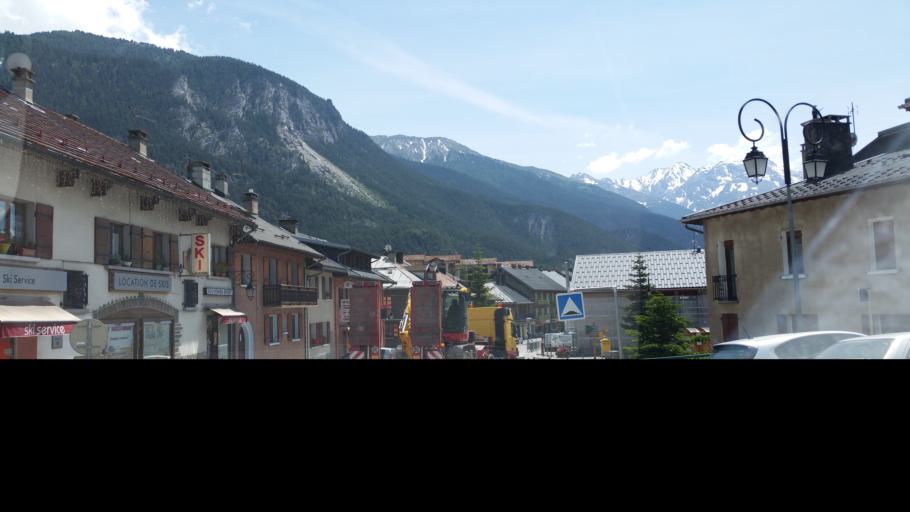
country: FR
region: Rhone-Alpes
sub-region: Departement de la Savoie
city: Modane
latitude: 45.2773
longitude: 6.8173
